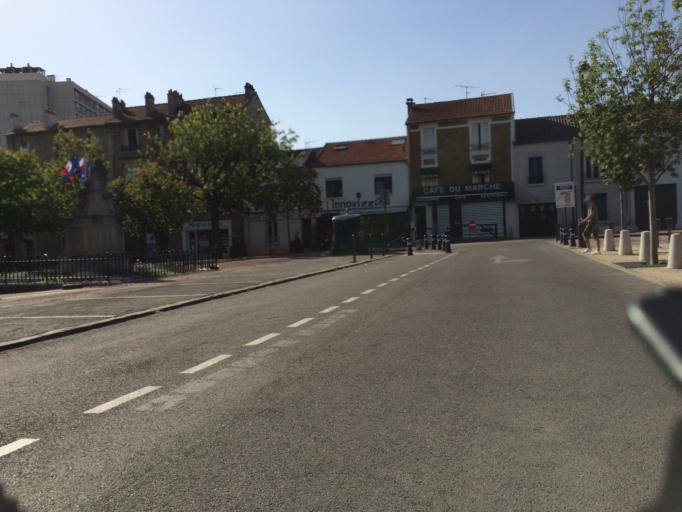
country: FR
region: Ile-de-France
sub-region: Departement des Hauts-de-Seine
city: Fontenay-aux-Roses
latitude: 48.7919
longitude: 2.2875
